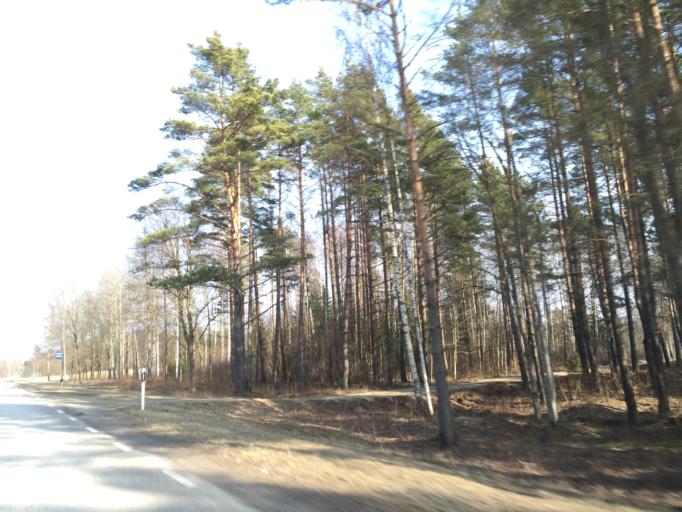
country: EE
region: Saare
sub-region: Kuressaare linn
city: Kuressaare
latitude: 58.3938
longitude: 22.7520
